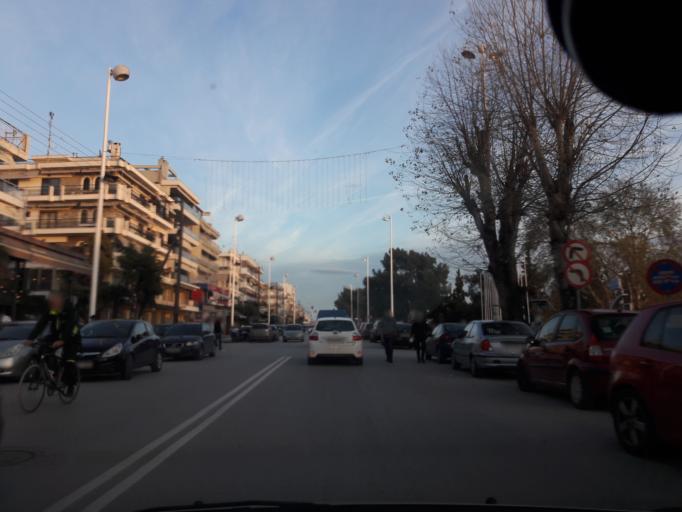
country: GR
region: Central Macedonia
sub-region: Nomos Thessalonikis
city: Kalamaria
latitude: 40.5766
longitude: 22.9460
